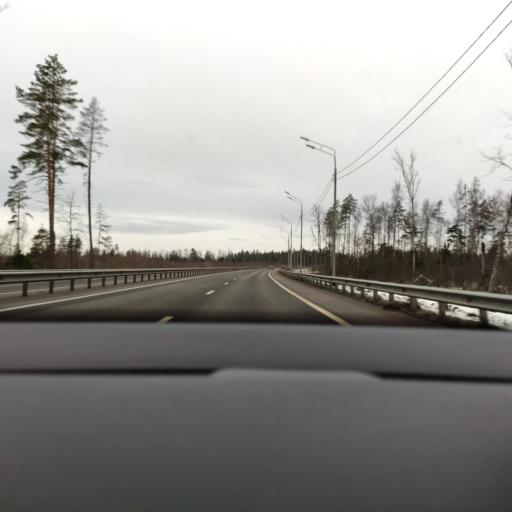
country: RU
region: Moskovskaya
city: Zvenigorod
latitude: 55.6734
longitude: 36.9076
